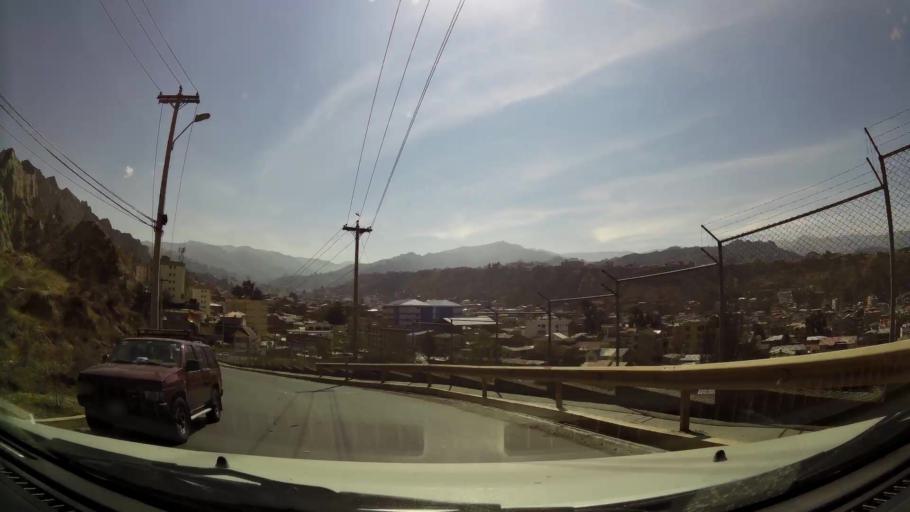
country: BO
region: La Paz
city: La Paz
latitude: -16.5236
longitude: -68.0914
